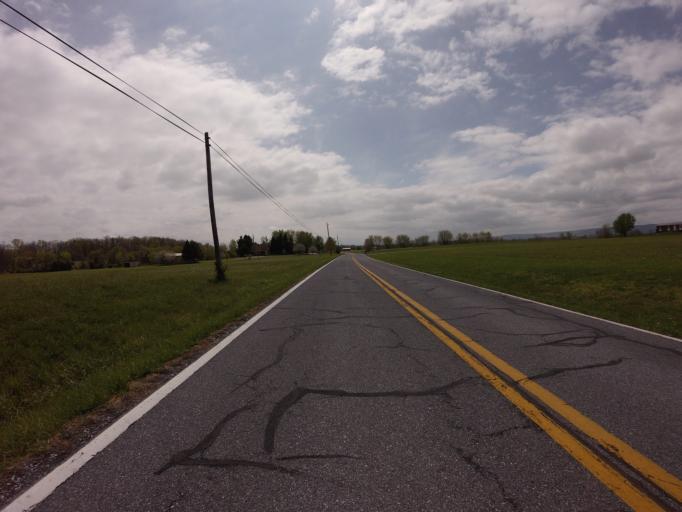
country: US
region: Maryland
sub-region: Frederick County
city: Thurmont
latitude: 39.6223
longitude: -77.3500
